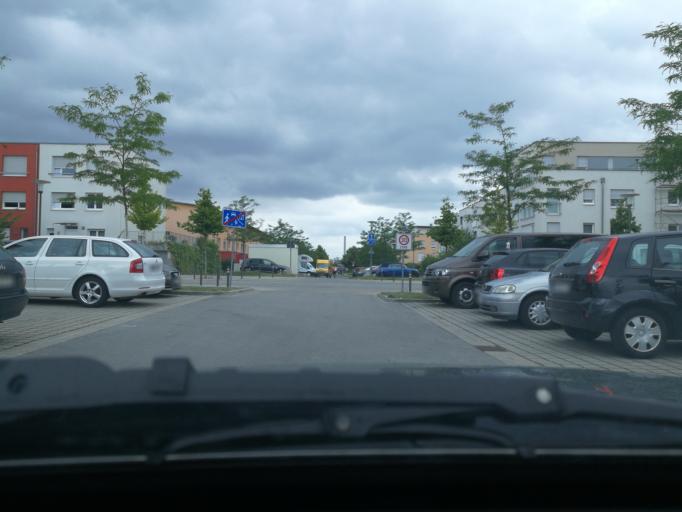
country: DE
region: Bavaria
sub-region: Regierungsbezirk Mittelfranken
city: Buckenhof
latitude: 49.5903
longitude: 11.0306
